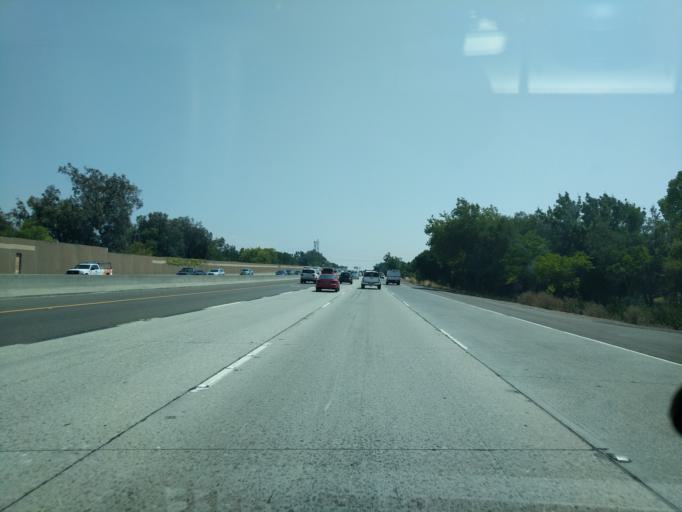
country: US
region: California
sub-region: Alameda County
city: Dublin
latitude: 37.7420
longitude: -121.9541
